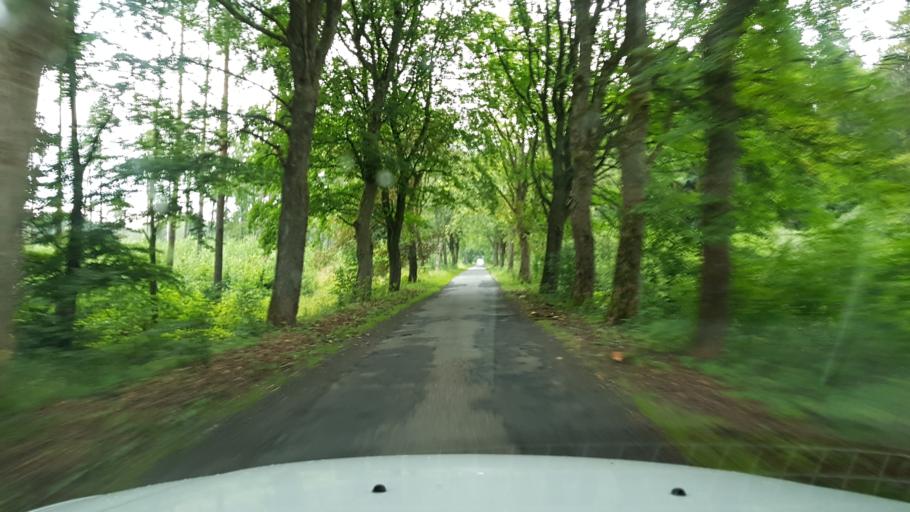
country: PL
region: West Pomeranian Voivodeship
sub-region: Powiat koszalinski
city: Bobolice
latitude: 53.9137
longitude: 16.6608
